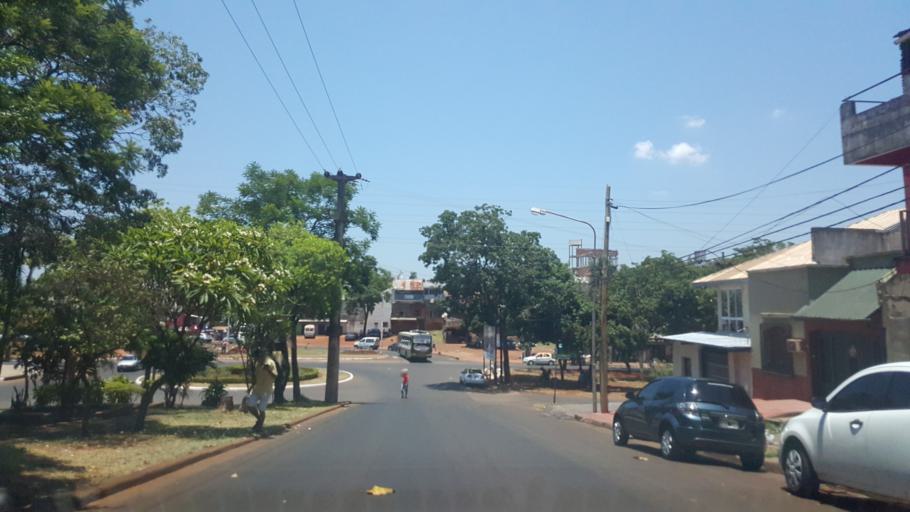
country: AR
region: Misiones
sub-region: Departamento de Capital
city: Posadas
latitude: -27.3747
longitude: -55.8883
